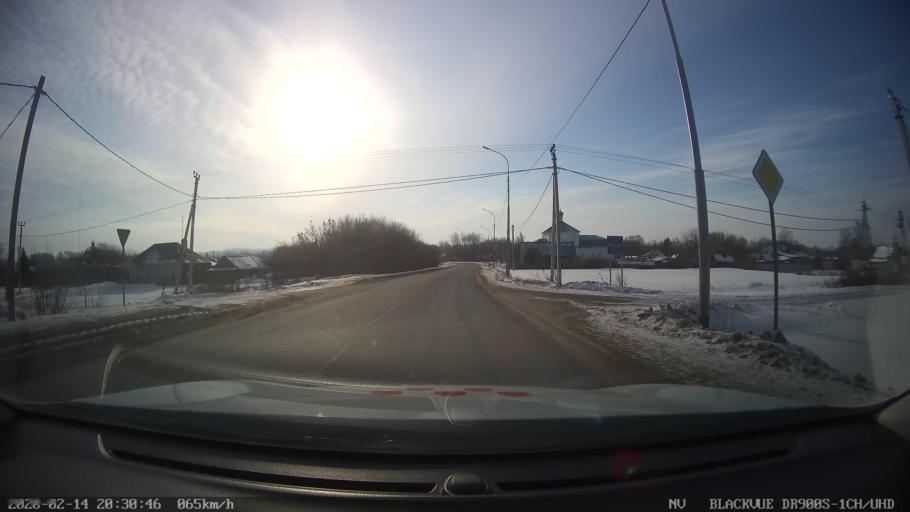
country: RU
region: Tatarstan
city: Stolbishchi
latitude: 55.4405
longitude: 48.9918
